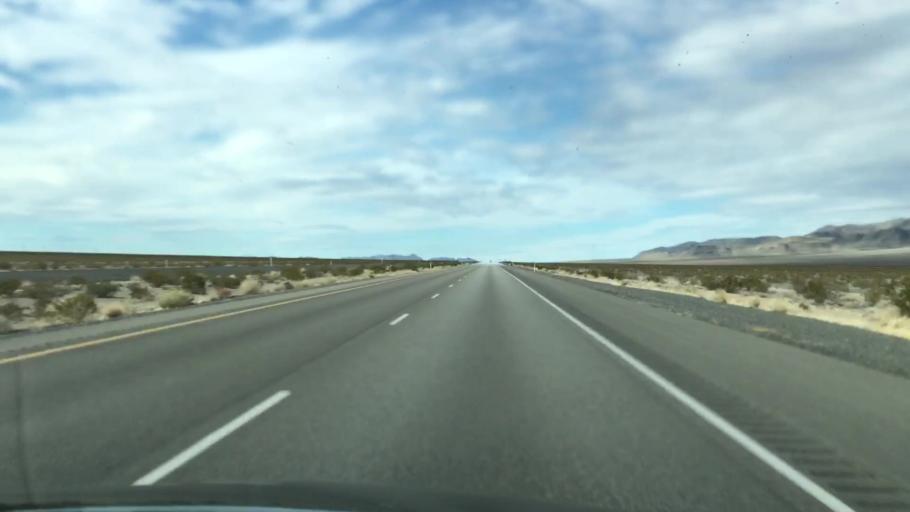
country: US
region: Nevada
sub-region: Nye County
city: Pahrump
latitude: 36.5778
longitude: -115.8874
